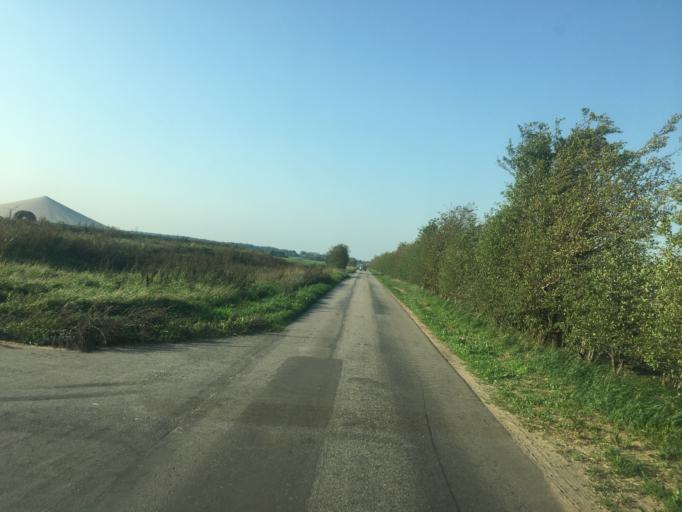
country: DE
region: Schleswig-Holstein
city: Ladelund
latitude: 54.9208
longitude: 9.0361
